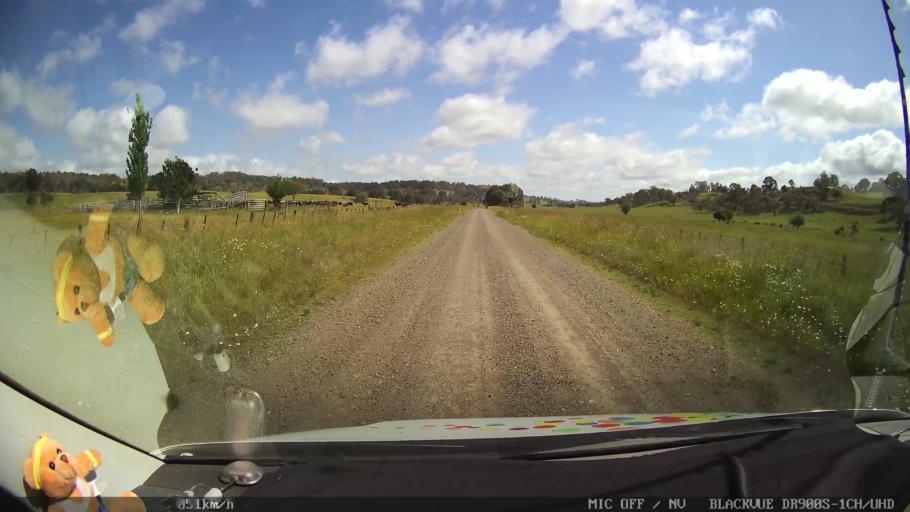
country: AU
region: New South Wales
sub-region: Glen Innes Severn
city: Glen Innes
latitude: -29.9715
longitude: 151.6994
